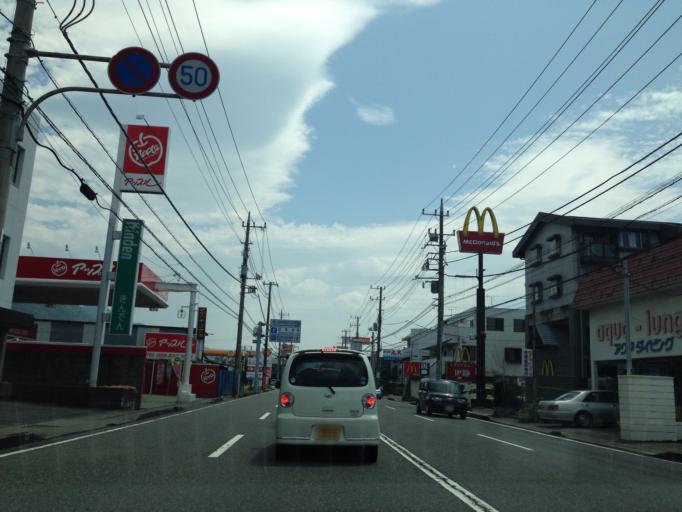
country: JP
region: Shizuoka
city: Numazu
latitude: 35.0874
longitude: 138.8675
